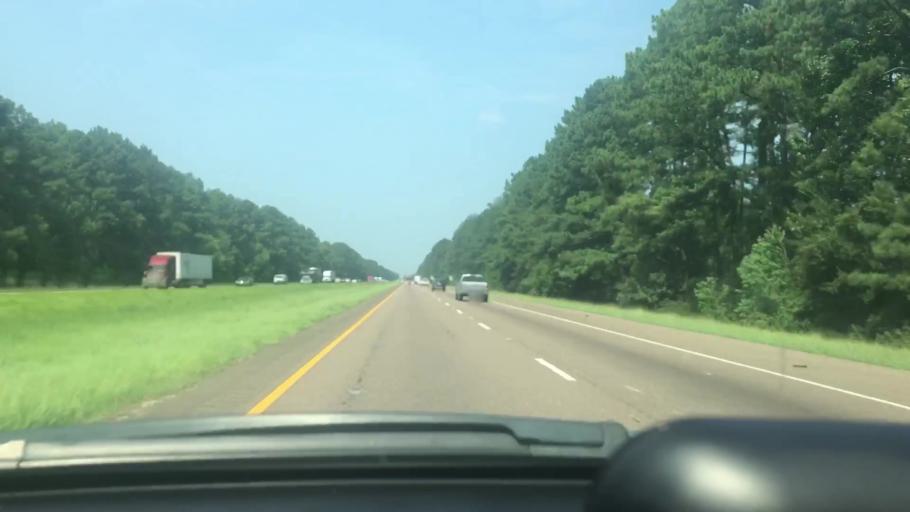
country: US
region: Louisiana
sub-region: Livingston Parish
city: Livingston
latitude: 30.4743
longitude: -90.7580
